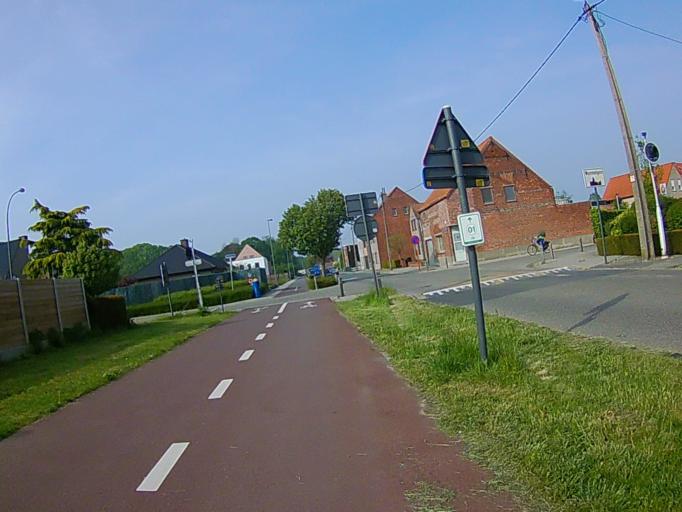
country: BE
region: Flanders
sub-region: Provincie Antwerpen
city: Wommelgem
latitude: 51.1937
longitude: 4.5269
